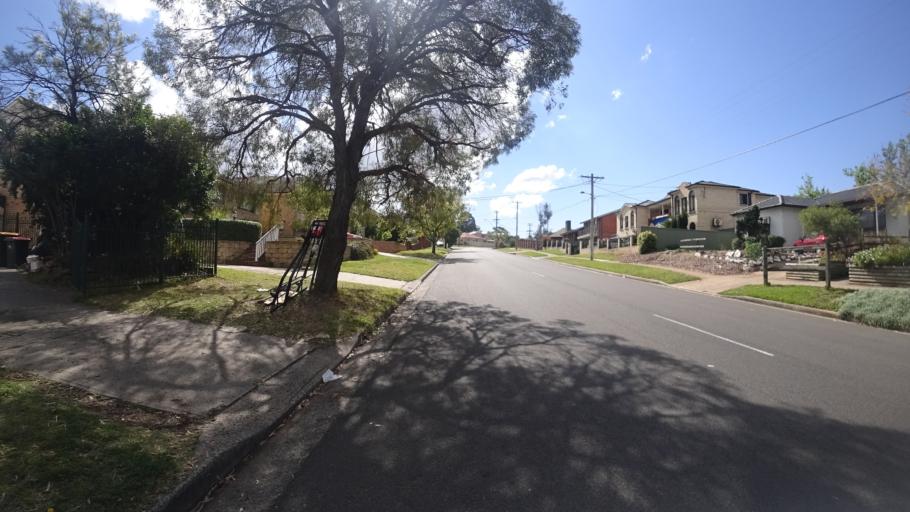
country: AU
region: New South Wales
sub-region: Fairfield
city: Cabramatta West
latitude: -33.9096
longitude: 150.9045
